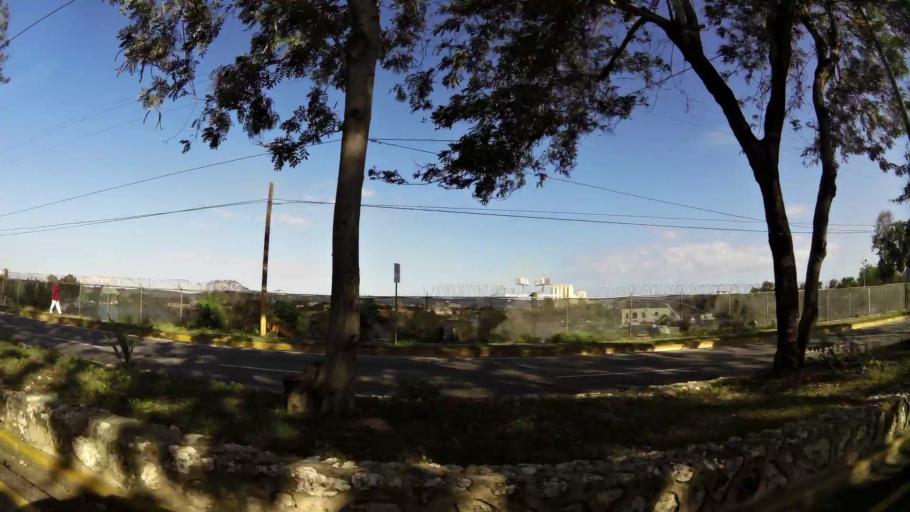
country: DO
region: Nacional
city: Ciudad Nueva
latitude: 18.4680
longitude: -69.8756
